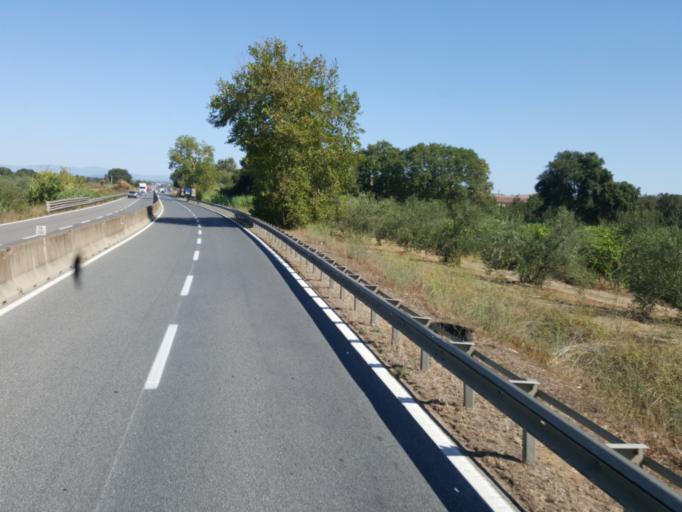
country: IT
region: Tuscany
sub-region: Provincia di Grosseto
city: Grosseto
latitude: 42.6694
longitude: 11.1423
